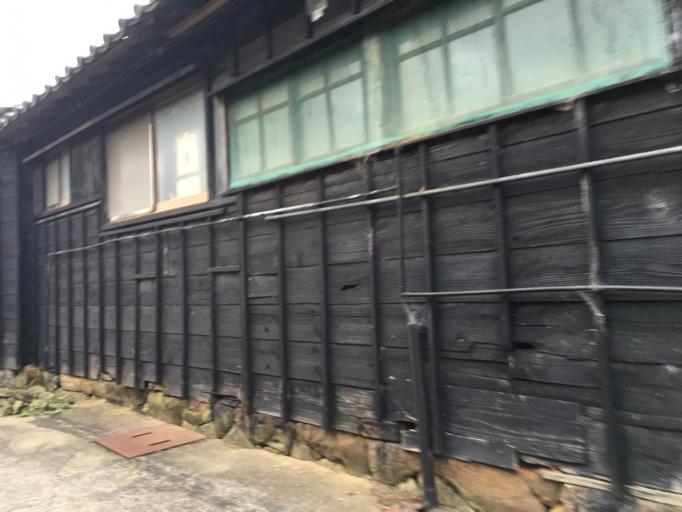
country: JP
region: Aichi
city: Ishiki
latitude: 34.7219
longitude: 137.0476
